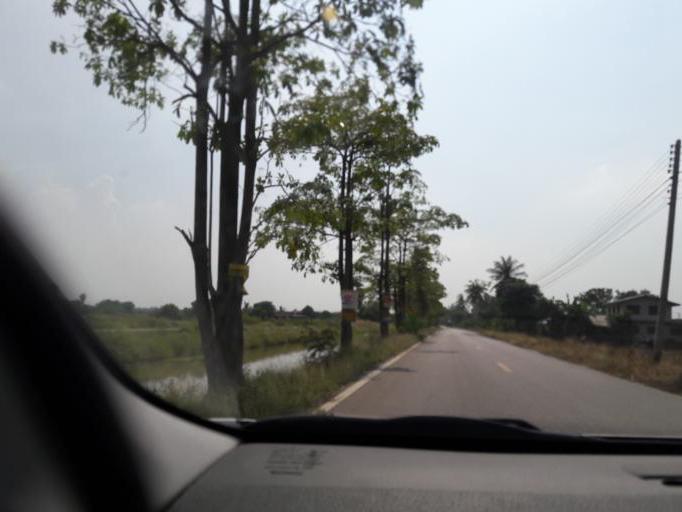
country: TH
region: Ang Thong
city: Ang Thong
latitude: 14.5853
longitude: 100.3978
